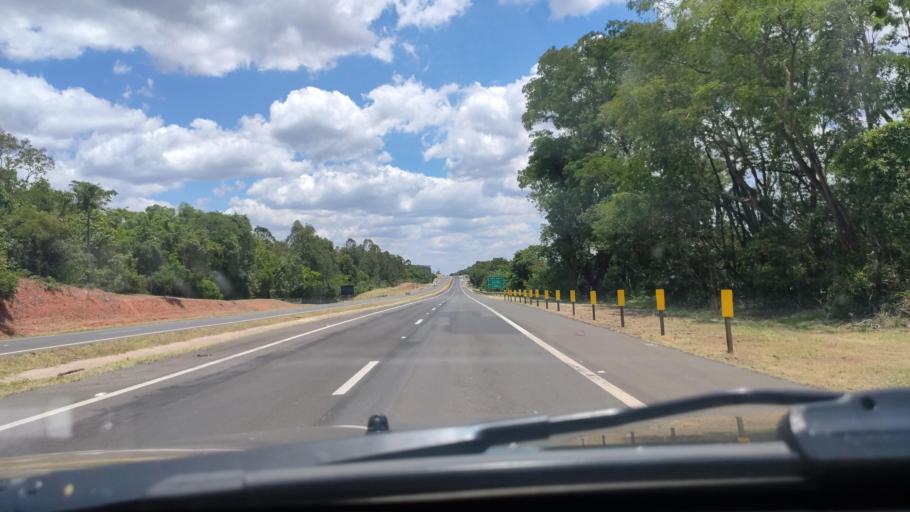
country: BR
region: Sao Paulo
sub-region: Duartina
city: Duartina
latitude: -22.5084
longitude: -49.2951
